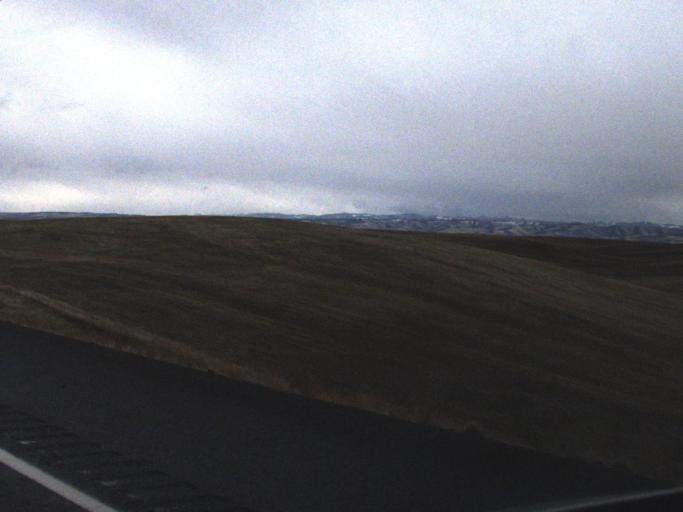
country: US
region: Washington
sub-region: Walla Walla County
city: Garrett
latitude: 46.0605
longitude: -118.4327
